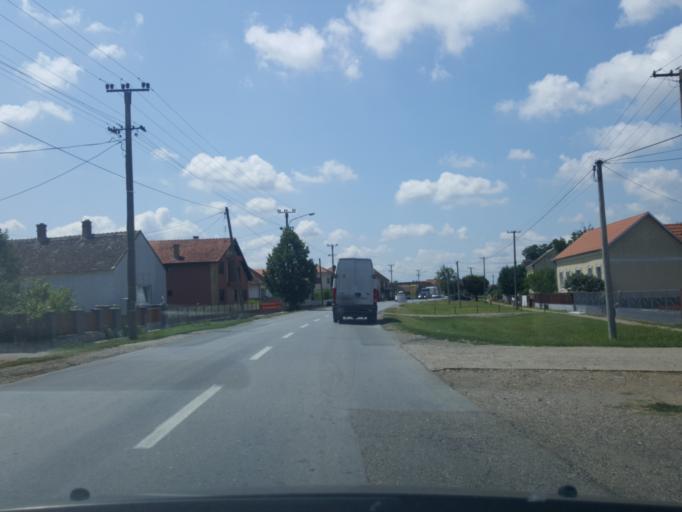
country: RS
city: Salas Nocajski
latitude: 44.9500
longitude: 19.5924
